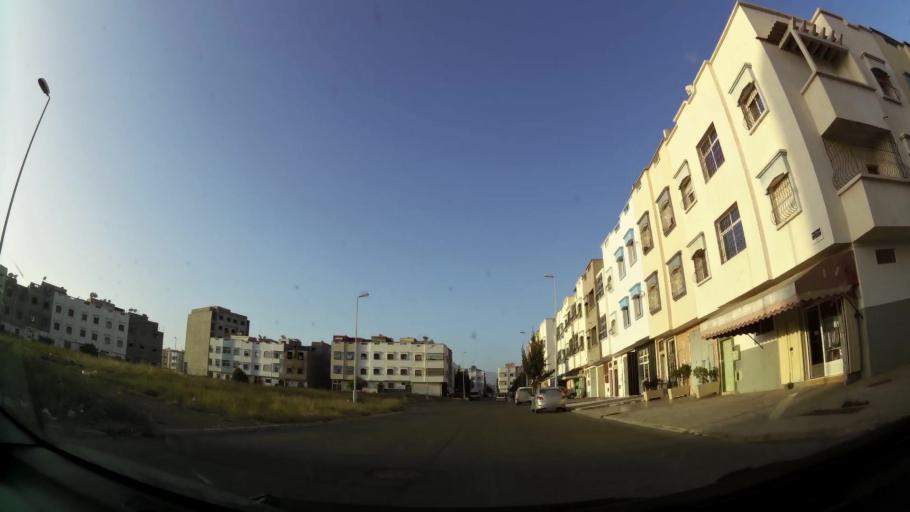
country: MA
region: Oued ed Dahab-Lagouira
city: Dakhla
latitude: 30.3991
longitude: -9.5620
